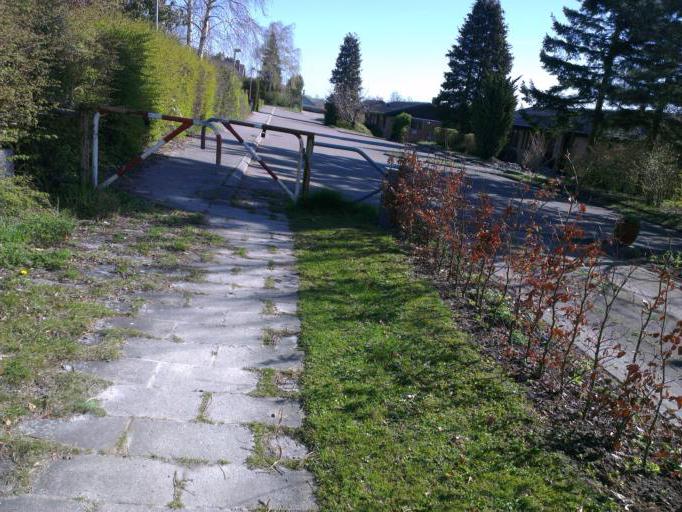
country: DK
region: Capital Region
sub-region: Frederikssund Kommune
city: Frederikssund
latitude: 55.8289
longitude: 12.0811
